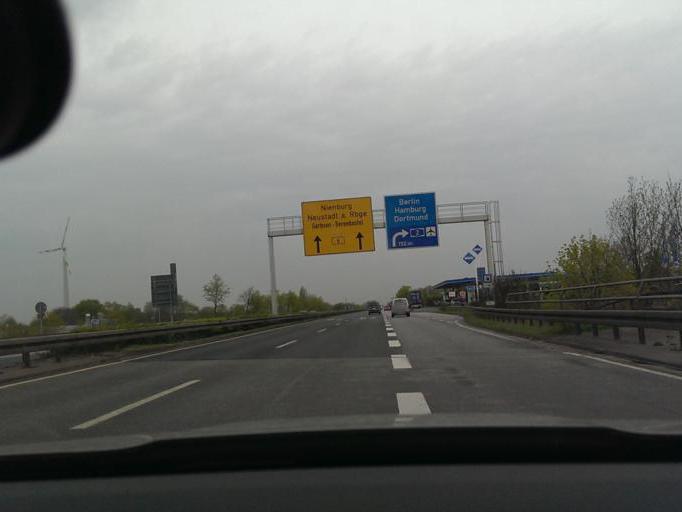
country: DE
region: Lower Saxony
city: Garbsen-Mitte
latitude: 52.4172
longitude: 9.6368
